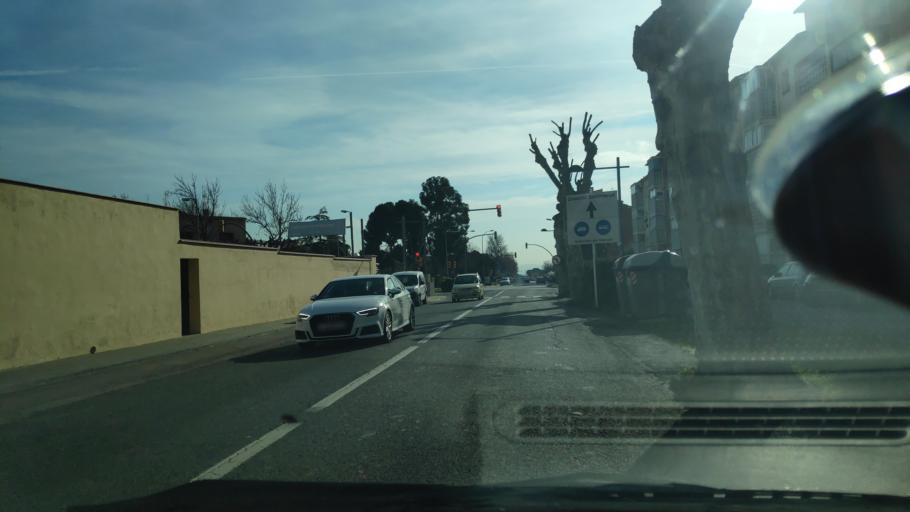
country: ES
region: Catalonia
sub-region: Provincia de Barcelona
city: Castellar del Valles
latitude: 41.6113
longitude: 2.0835
